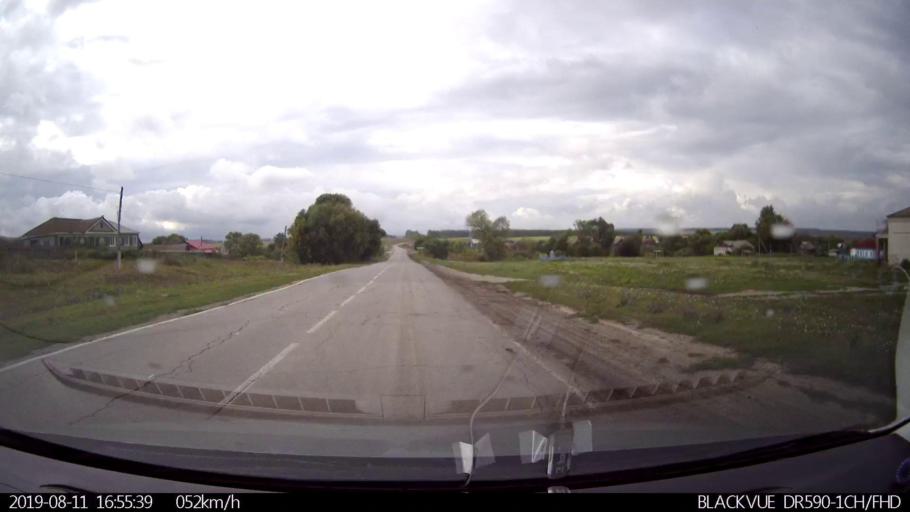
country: RU
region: Ulyanovsk
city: Mayna
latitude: 54.2831
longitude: 47.6616
